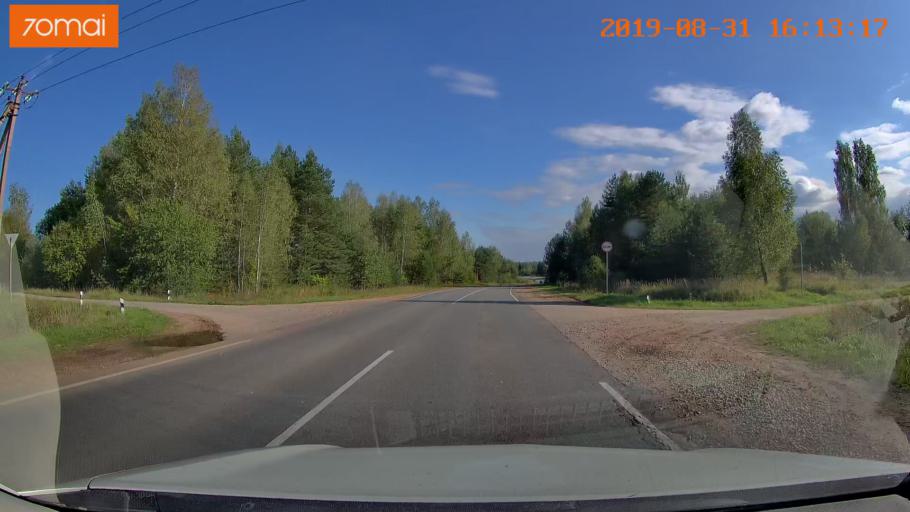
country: RU
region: Kaluga
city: Nikola-Lenivets
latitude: 54.5786
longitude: 35.4440
